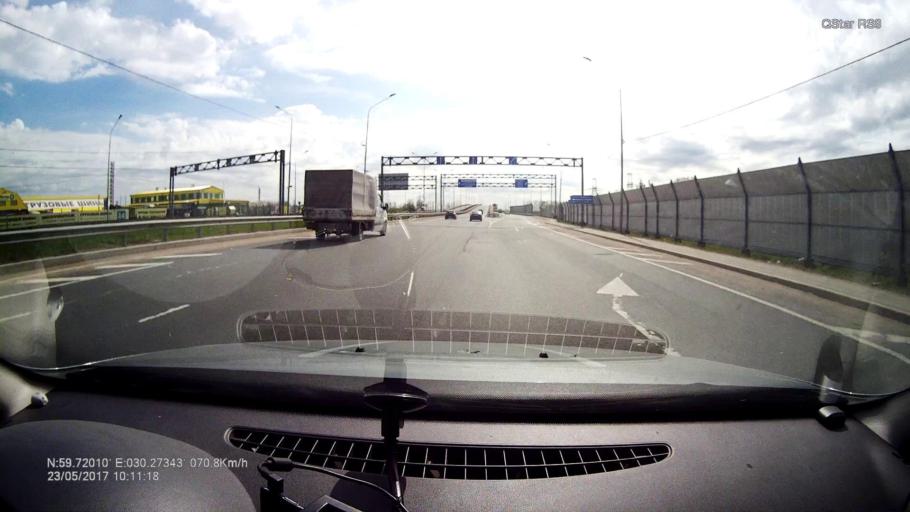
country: RU
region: St.-Petersburg
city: Aleksandrovskaya
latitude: 59.7200
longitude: 30.2738
